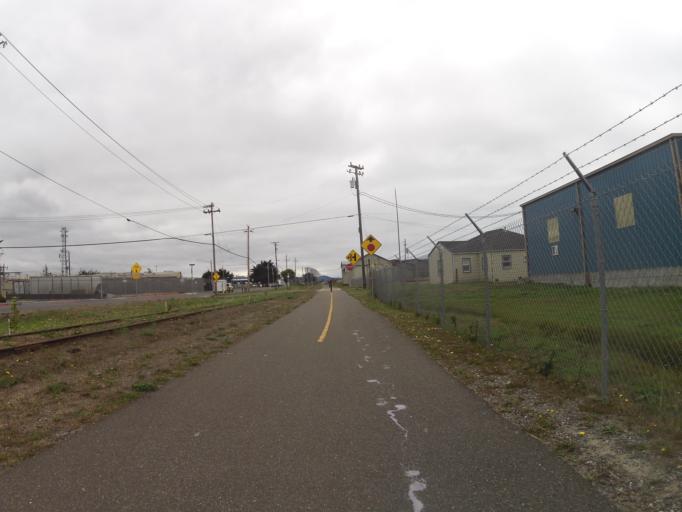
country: US
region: California
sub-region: Humboldt County
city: Eureka
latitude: 40.7947
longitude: -124.1839
